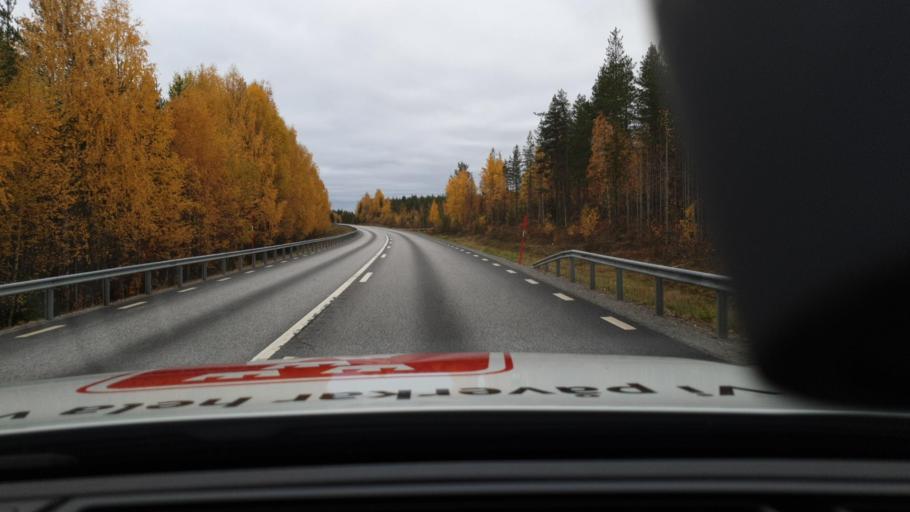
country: SE
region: Norrbotten
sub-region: Overkalix Kommun
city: OEverkalix
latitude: 66.6467
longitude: 22.1866
